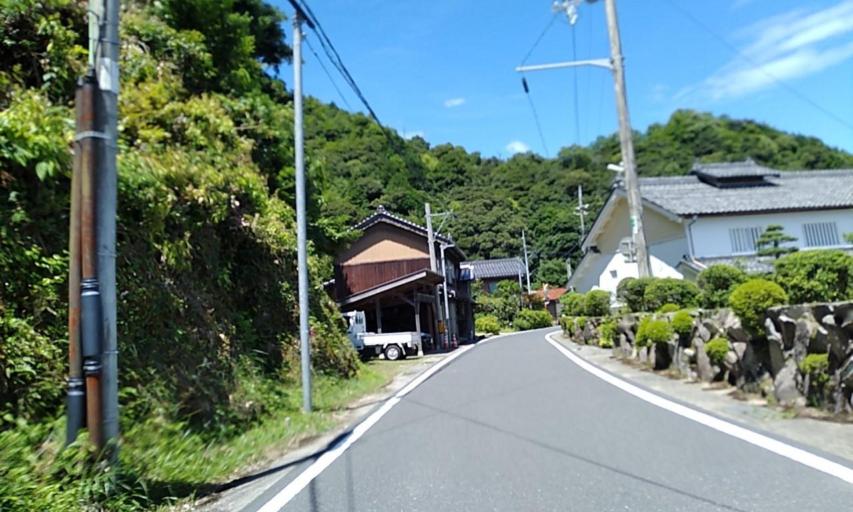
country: JP
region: Kyoto
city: Miyazu
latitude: 35.6702
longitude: 135.2741
